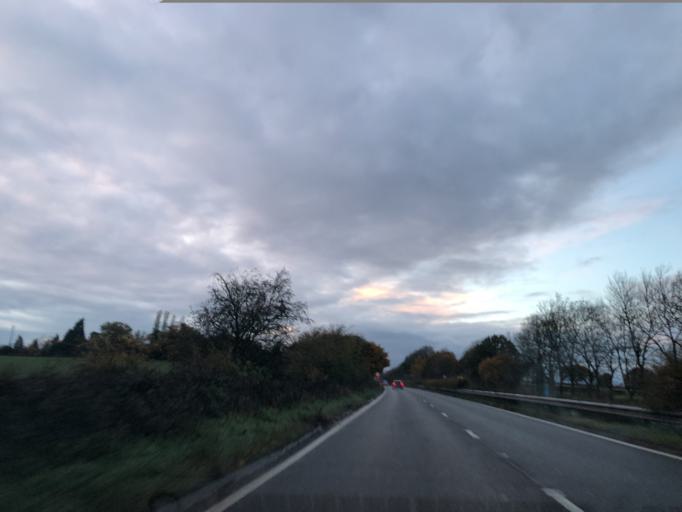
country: GB
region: England
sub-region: Solihull
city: Meriden
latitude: 52.4374
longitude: -1.6118
